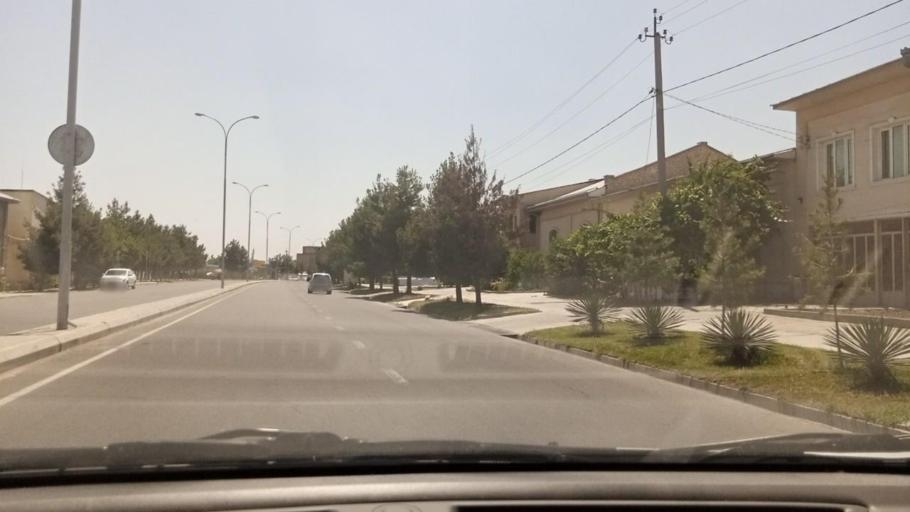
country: UZ
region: Toshkent Shahri
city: Tashkent
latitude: 41.2300
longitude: 69.1838
